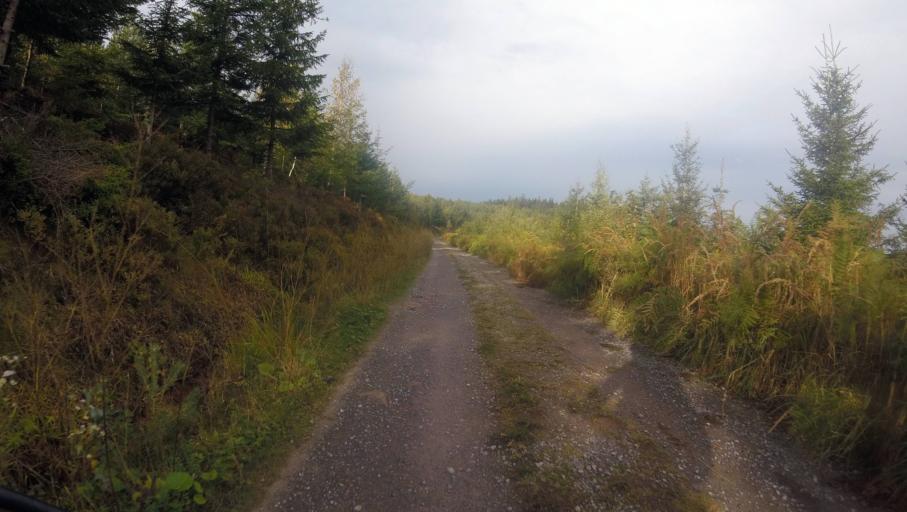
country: DE
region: Baden-Wuerttemberg
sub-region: Karlsruhe Region
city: Loffenau
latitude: 48.7457
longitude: 8.4212
